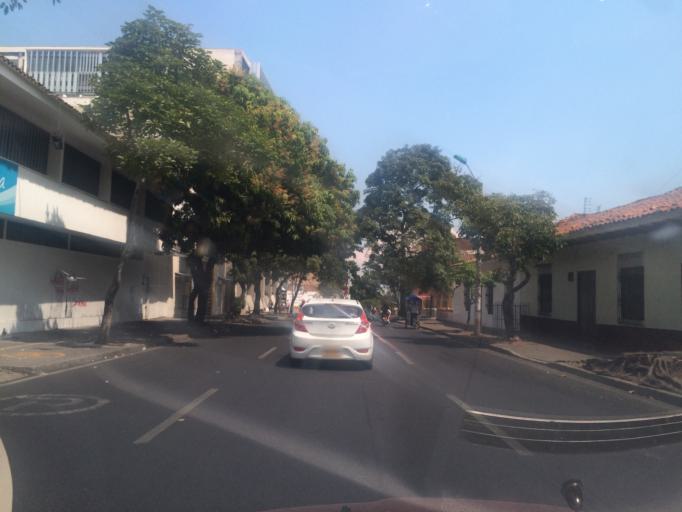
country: CO
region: Valle del Cauca
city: Cali
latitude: 3.4484
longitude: -76.5344
